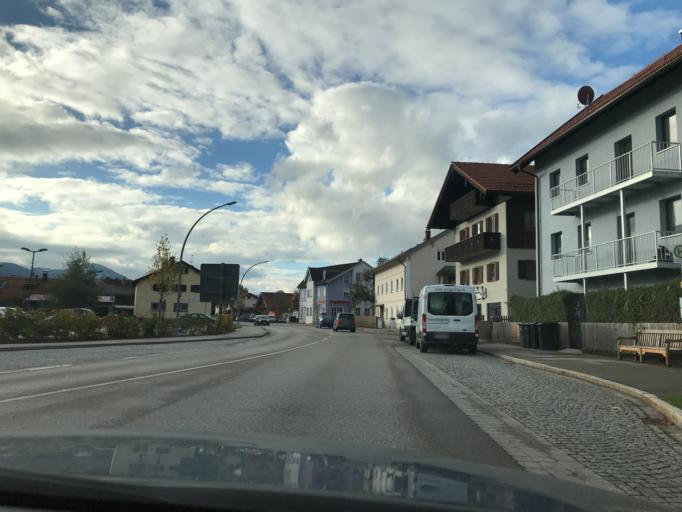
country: DE
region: Bavaria
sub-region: Upper Bavaria
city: Bad Toelz
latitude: 47.7564
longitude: 11.5599
